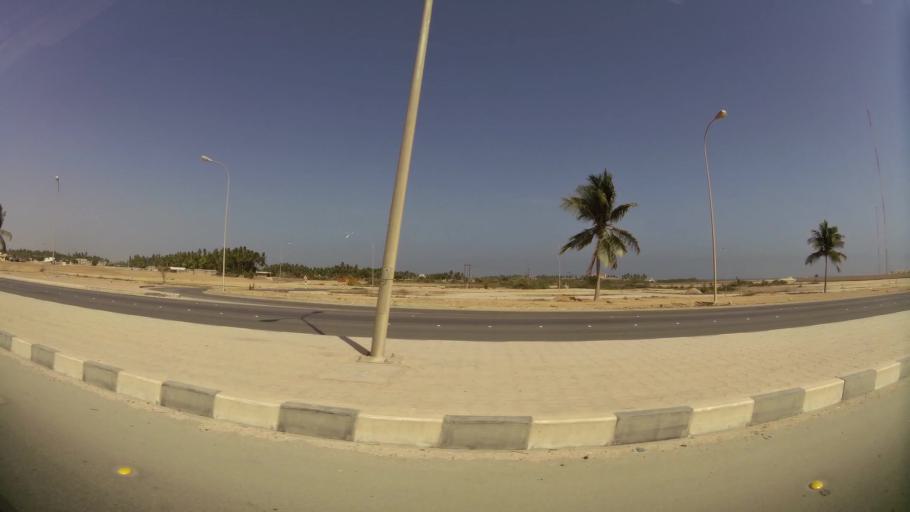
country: OM
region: Zufar
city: Salalah
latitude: 16.9964
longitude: 54.0319
